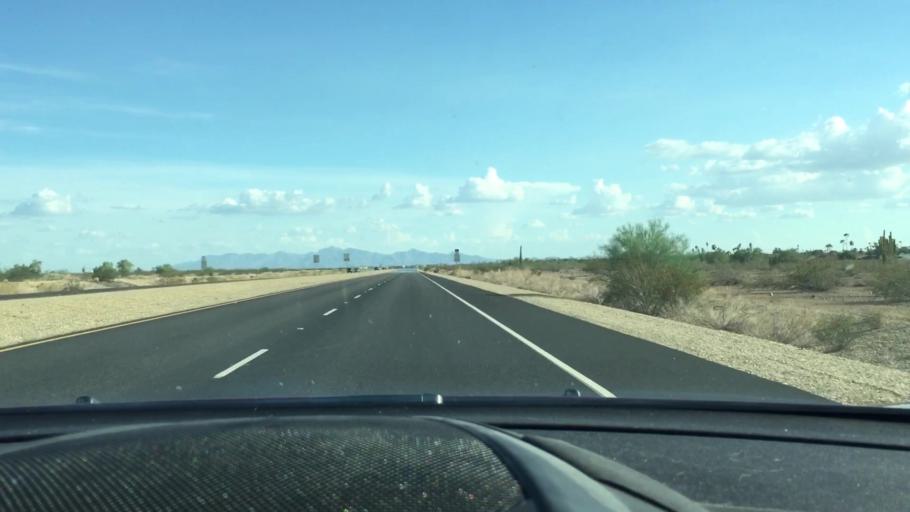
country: US
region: Arizona
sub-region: Maricopa County
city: Sun City West
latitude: 33.6770
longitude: -112.3234
